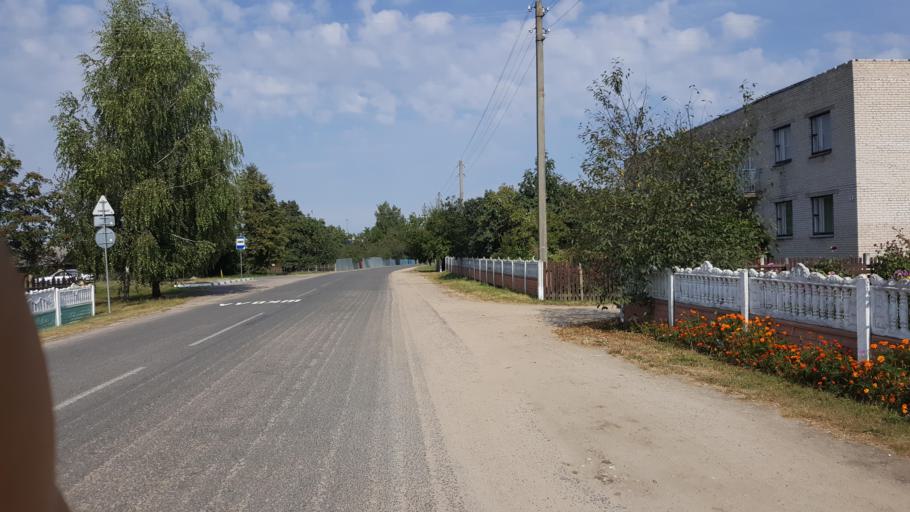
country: BY
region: Brest
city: Kamyanyets
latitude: 52.4678
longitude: 23.7312
